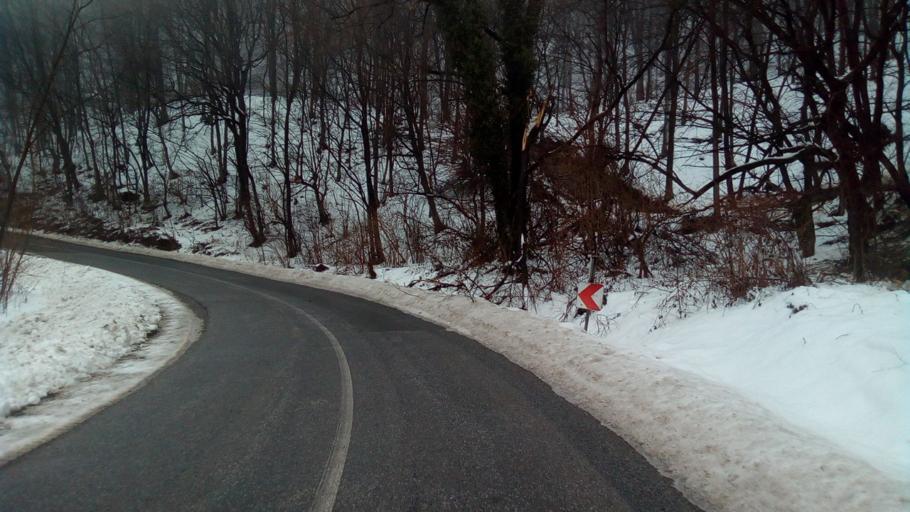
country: HR
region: Sisacko-Moslavacka
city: Petrinja
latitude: 45.3779
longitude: 16.2878
